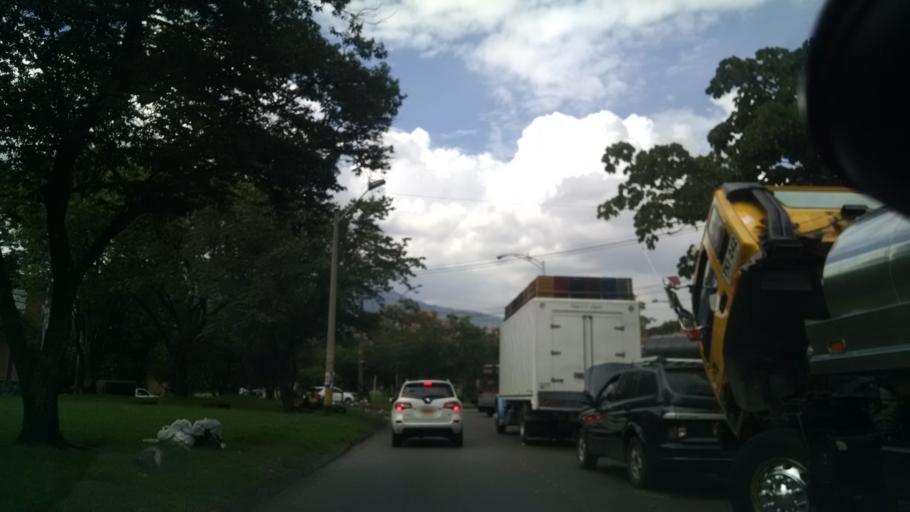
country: CO
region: Antioquia
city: Medellin
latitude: 6.2487
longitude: -75.5791
